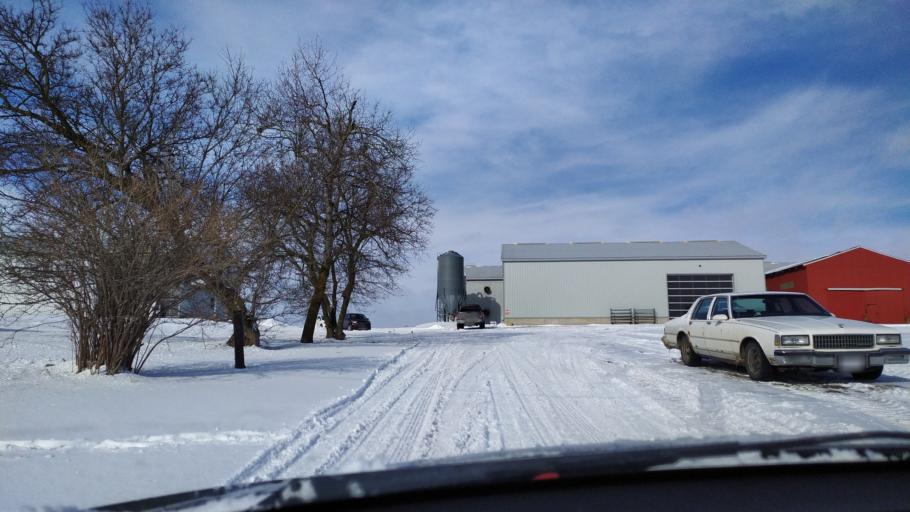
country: CA
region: Ontario
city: Waterloo
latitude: 43.4700
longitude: -80.7370
